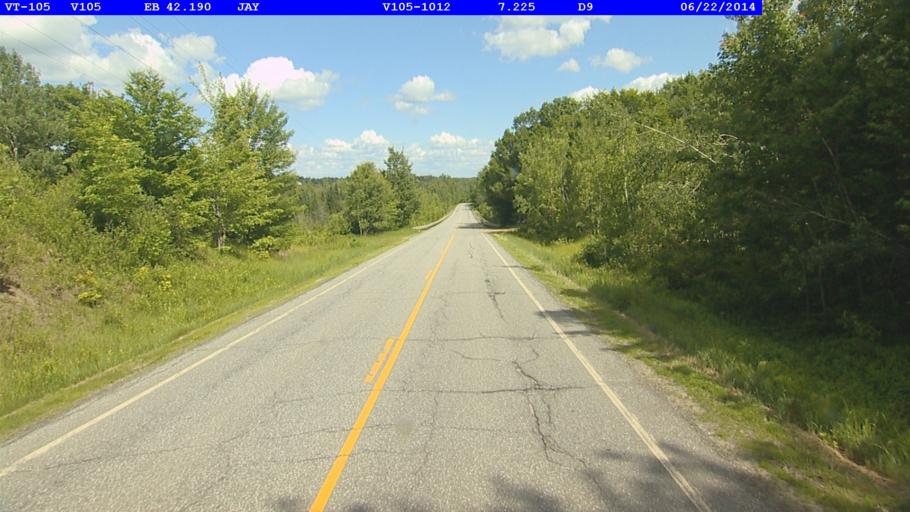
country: CA
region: Quebec
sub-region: Monteregie
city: Sutton
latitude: 44.9688
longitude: -72.4442
